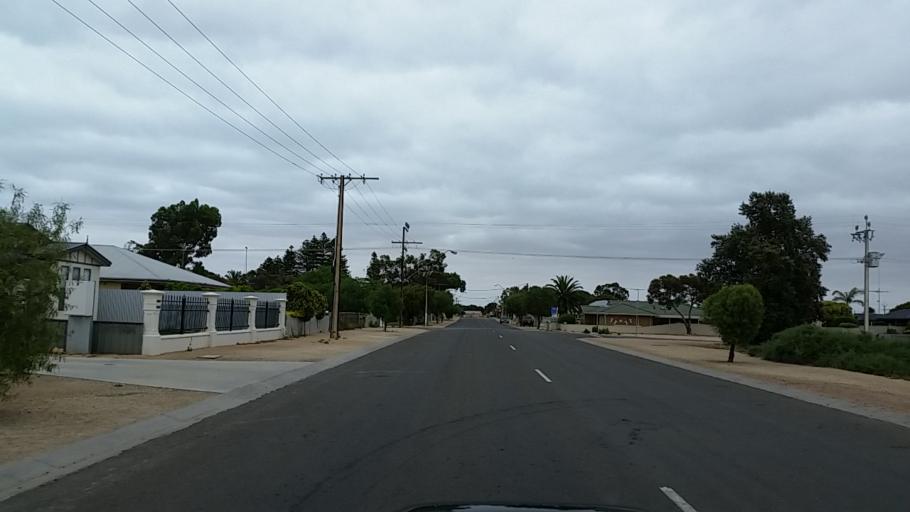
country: AU
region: South Australia
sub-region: Wakefield
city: Balaklava
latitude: -34.1853
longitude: 138.1527
